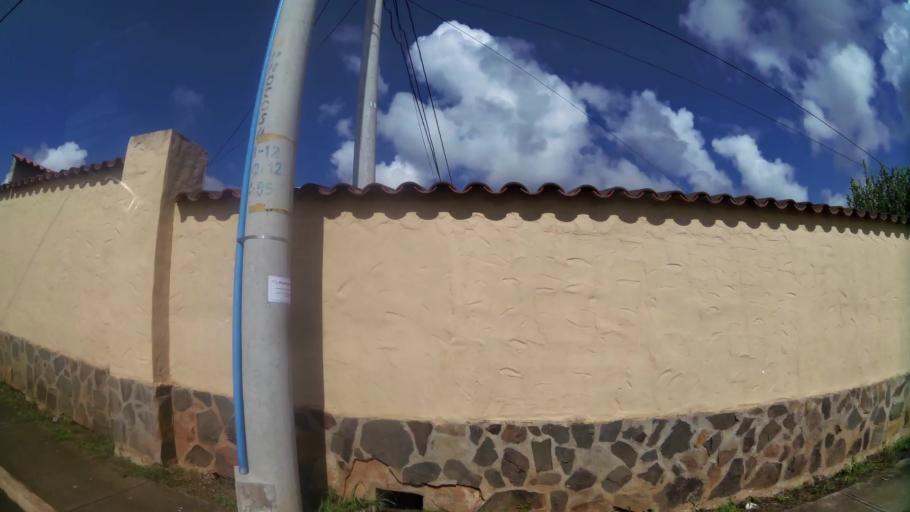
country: PA
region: Panama
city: Nuevo Arraijan
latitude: 8.9019
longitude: -79.7435
